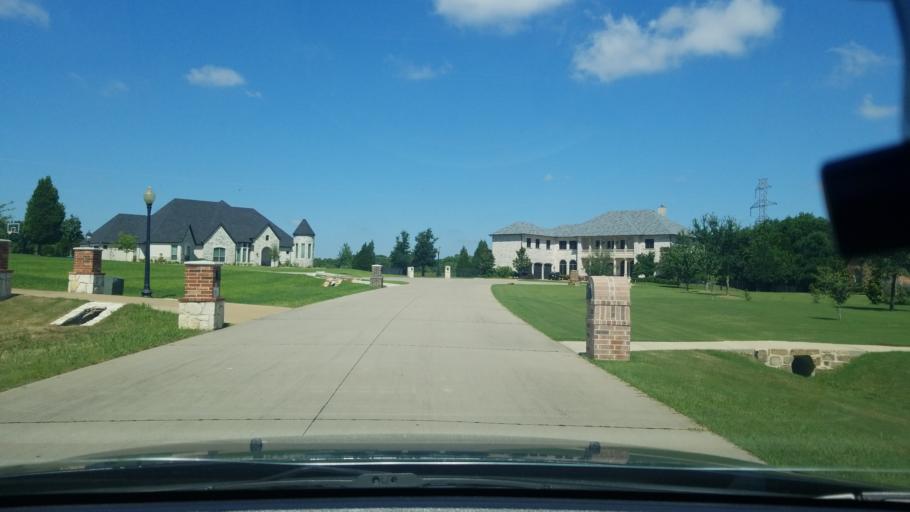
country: US
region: Texas
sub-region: Dallas County
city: Sunnyvale
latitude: 32.7970
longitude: -96.5715
